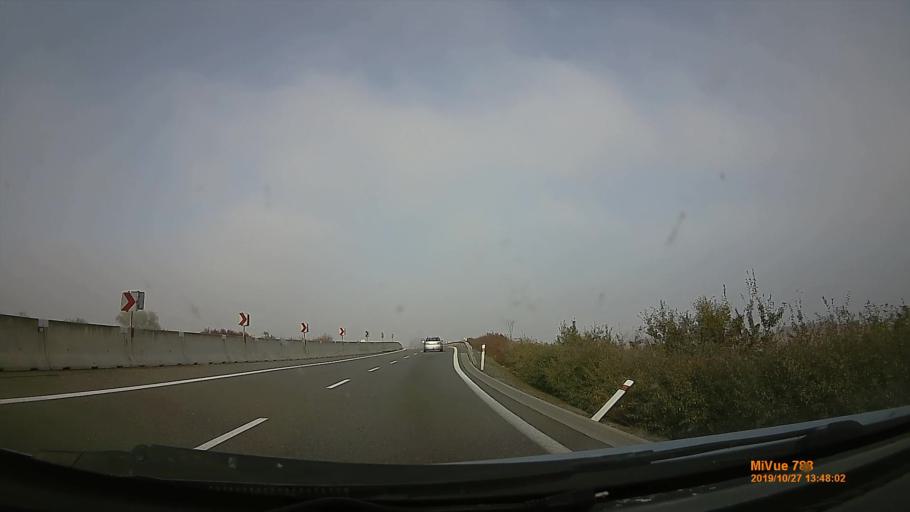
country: CZ
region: Olomoucky
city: Hnevotin
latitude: 49.5960
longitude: 17.1986
